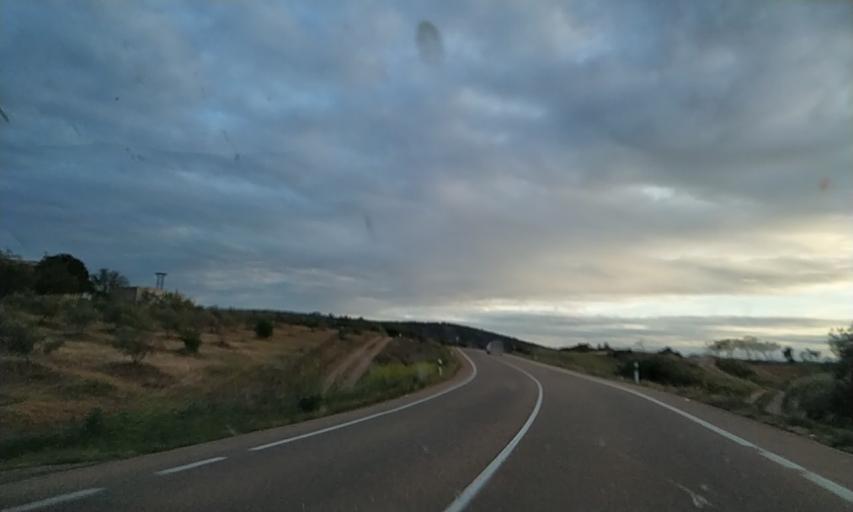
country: ES
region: Extremadura
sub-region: Provincia de Badajoz
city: Puebla de Obando
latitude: 39.1830
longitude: -6.6078
